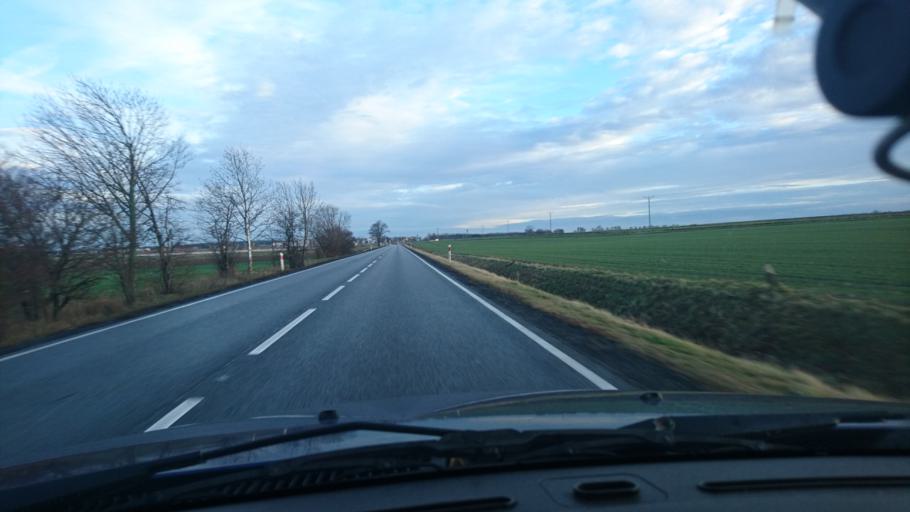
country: PL
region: Greater Poland Voivodeship
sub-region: Powiat kepinski
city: Slupia pod Kepnem
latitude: 51.2344
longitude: 18.0581
